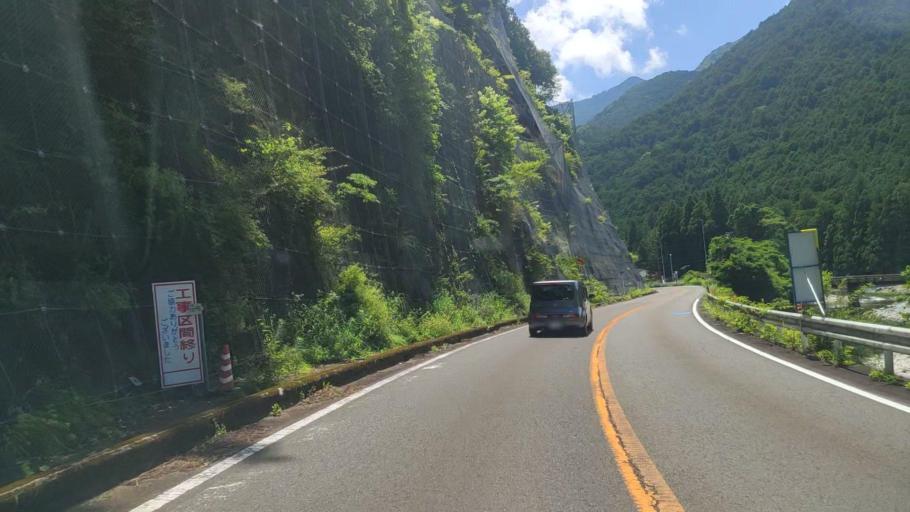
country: JP
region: Mie
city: Owase
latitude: 33.9811
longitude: 136.1063
